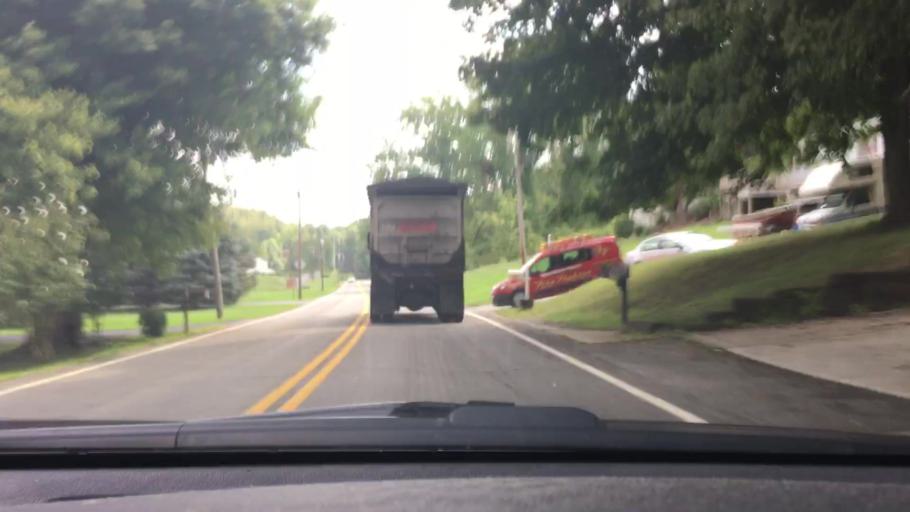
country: US
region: Pennsylvania
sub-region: Washington County
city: Gastonville
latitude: 40.2550
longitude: -79.9708
